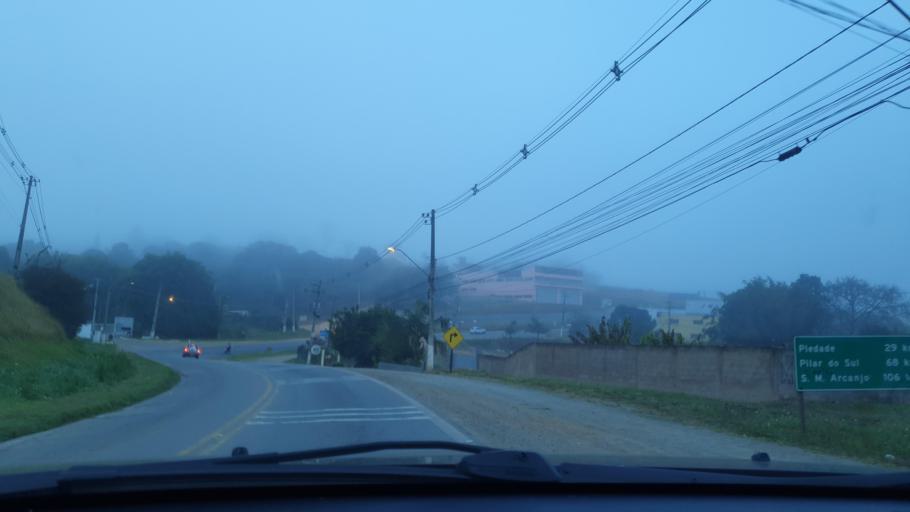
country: BR
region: Sao Paulo
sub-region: Ibiuna
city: Ibiuna
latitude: -23.6652
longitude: -47.2271
